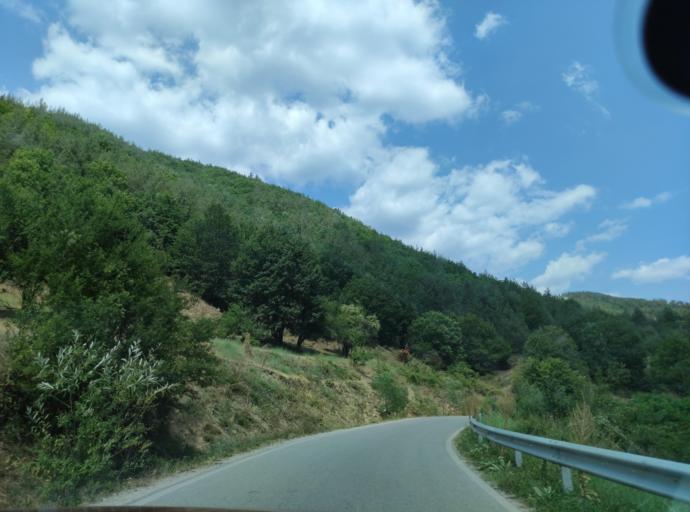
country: BG
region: Blagoevgrad
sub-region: Obshtina Belitsa
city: Belitsa
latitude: 42.0035
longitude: 23.5513
